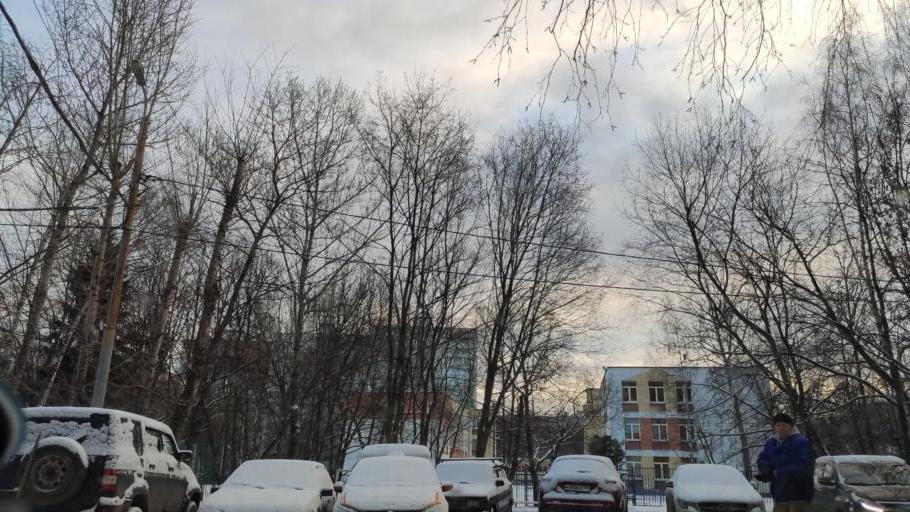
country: RU
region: Moskovskaya
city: Biryulevo Zapadnoye
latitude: 55.6006
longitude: 37.6537
